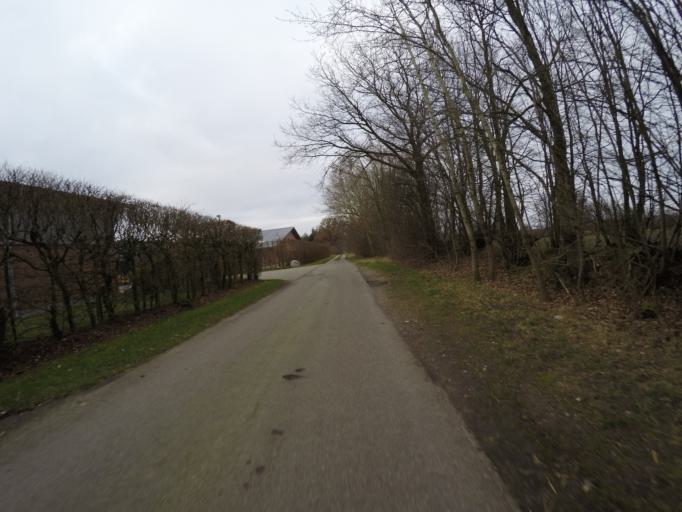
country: DE
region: Schleswig-Holstein
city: Hemdingen
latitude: 53.7722
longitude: 9.8426
